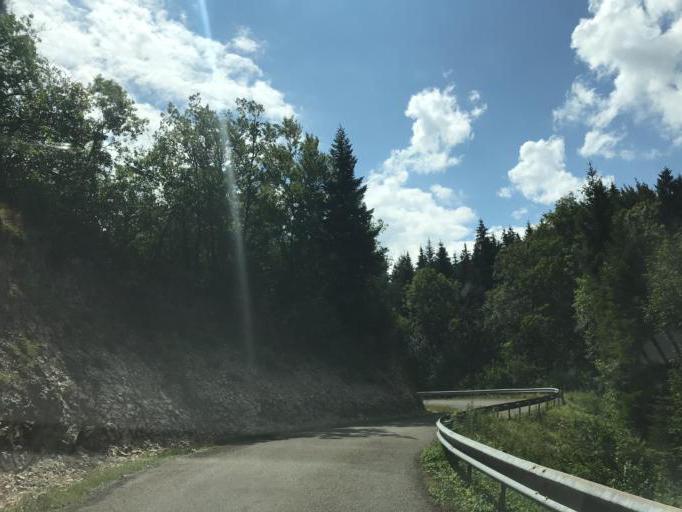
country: FR
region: Franche-Comte
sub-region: Departement du Jura
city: Moirans-en-Montagne
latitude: 46.4951
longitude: 5.7746
